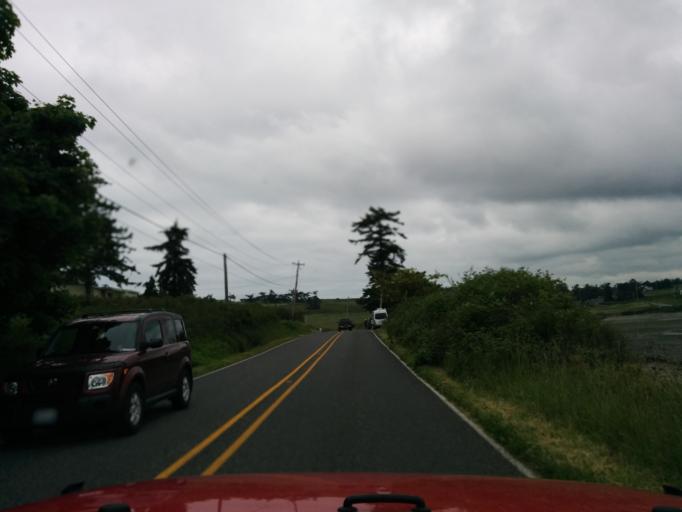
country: US
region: Washington
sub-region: Island County
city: Coupeville
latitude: 48.2294
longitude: -122.7349
